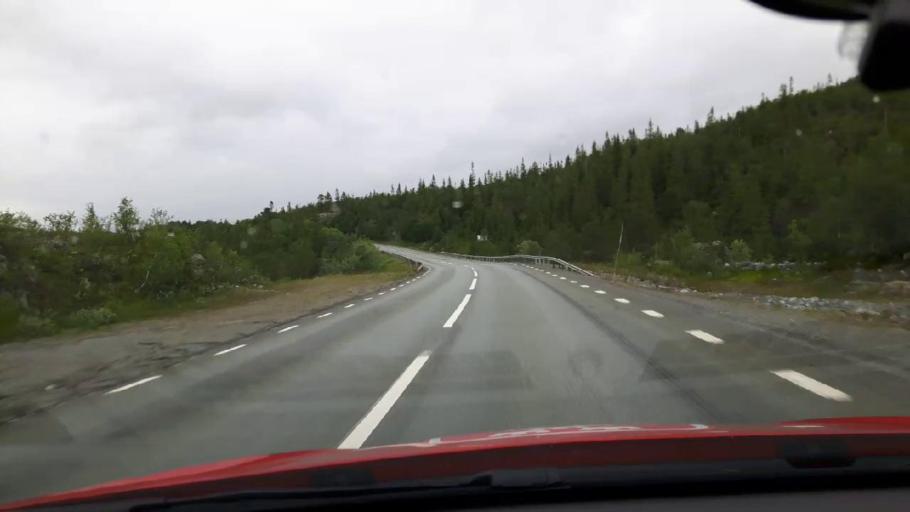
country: NO
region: Nord-Trondelag
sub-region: Meraker
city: Meraker
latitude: 63.3243
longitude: 12.0664
